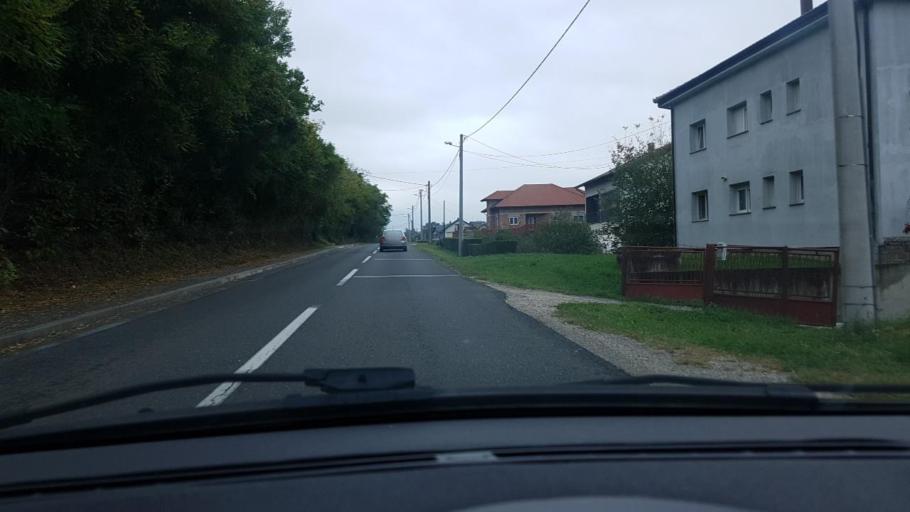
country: HR
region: Grad Zagreb
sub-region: Sesvete
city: Sesvete
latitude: 45.8902
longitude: 16.1204
